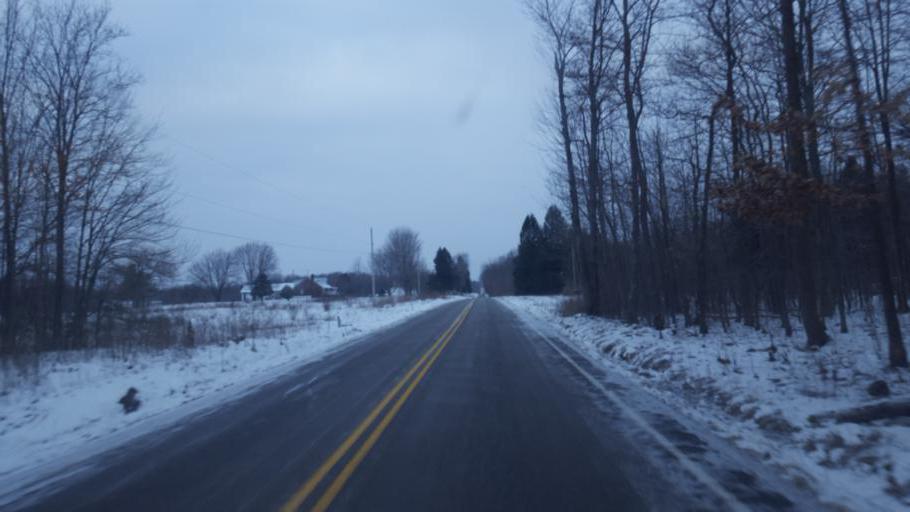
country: US
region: Pennsylvania
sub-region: Mercer County
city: Stoneboro
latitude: 41.4051
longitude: -80.0167
